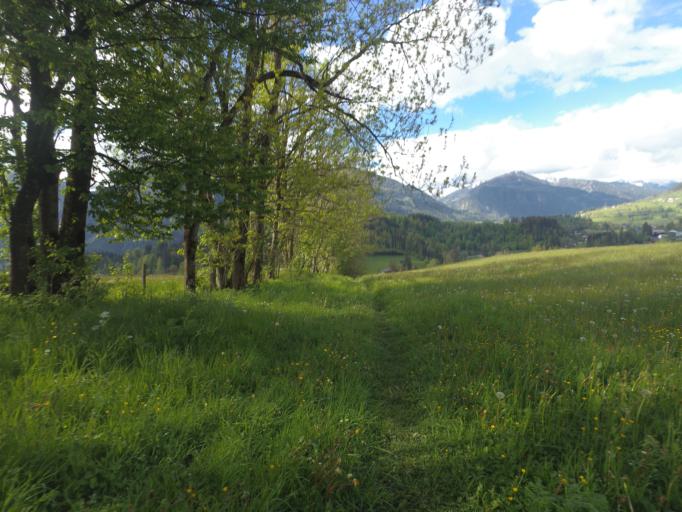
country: AT
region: Salzburg
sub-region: Politischer Bezirk Sankt Johann im Pongau
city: Goldegg
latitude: 47.3206
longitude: 13.1084
